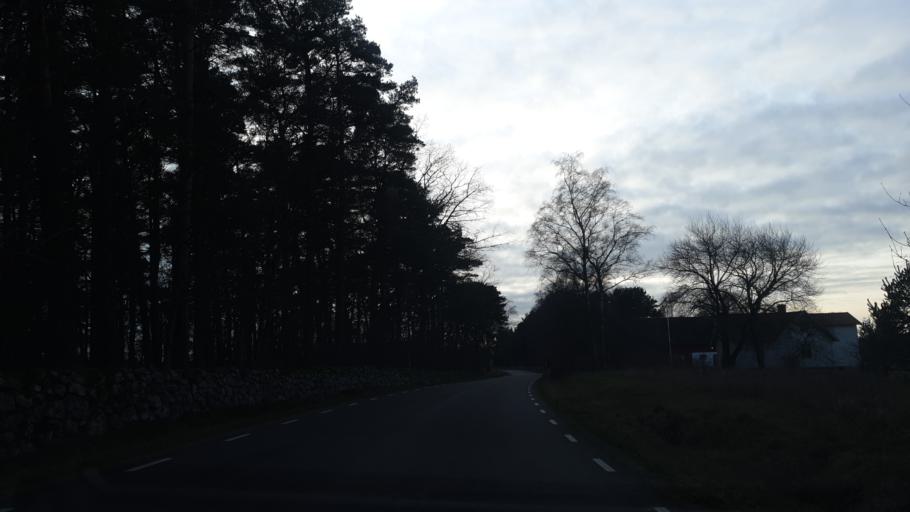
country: SE
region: Kalmar
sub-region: Torsas Kommun
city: Torsas
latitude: 56.2315
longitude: 15.9971
